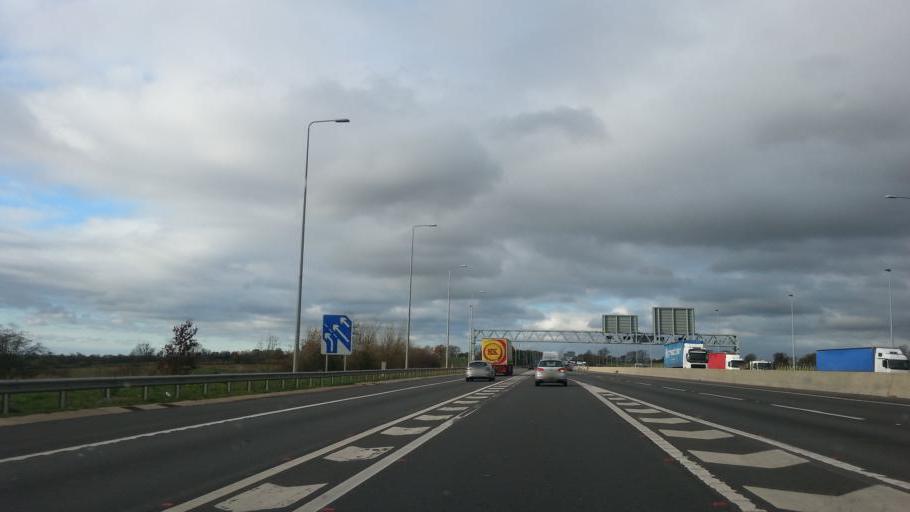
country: GB
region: England
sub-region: Leicestershire
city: Lutterworth
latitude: 52.4050
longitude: -1.1866
